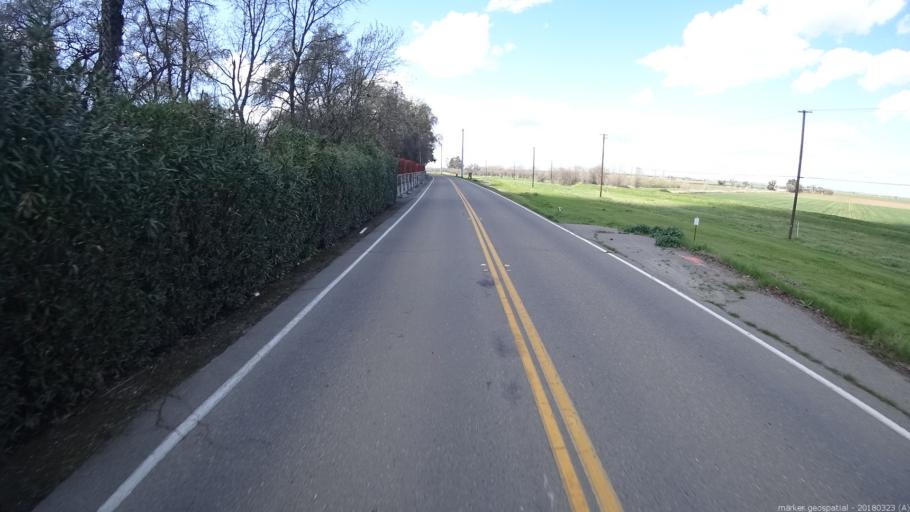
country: US
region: California
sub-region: Yolo County
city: West Sacramento
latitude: 38.6487
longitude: -121.5690
